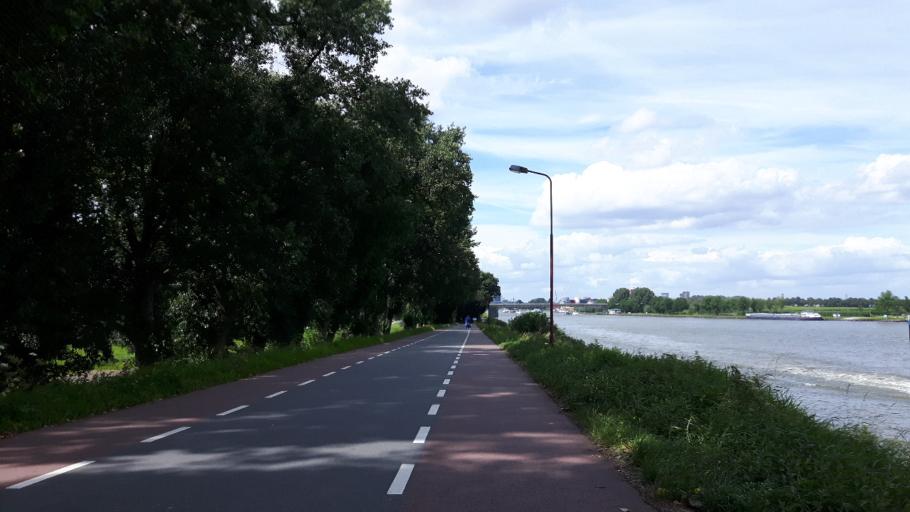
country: NL
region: Utrecht
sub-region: Gemeente Nieuwegein
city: Nieuwegein
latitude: 52.0348
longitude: 5.1113
